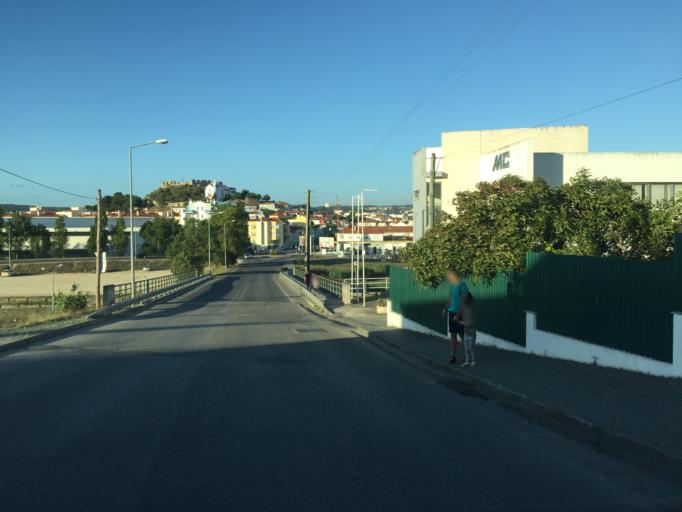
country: PT
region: Lisbon
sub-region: Torres Vedras
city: Torres Vedras
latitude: 39.0903
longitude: -9.2657
